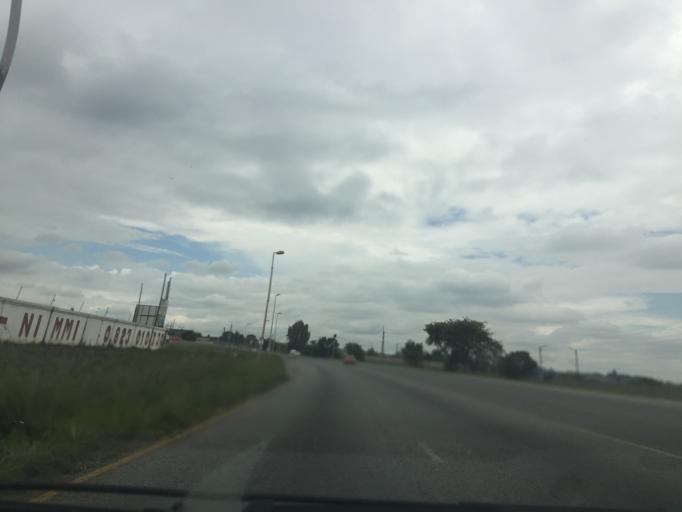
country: ZA
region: Gauteng
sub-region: City of Johannesburg Metropolitan Municipality
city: Midrand
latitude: -26.0070
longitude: 28.1356
